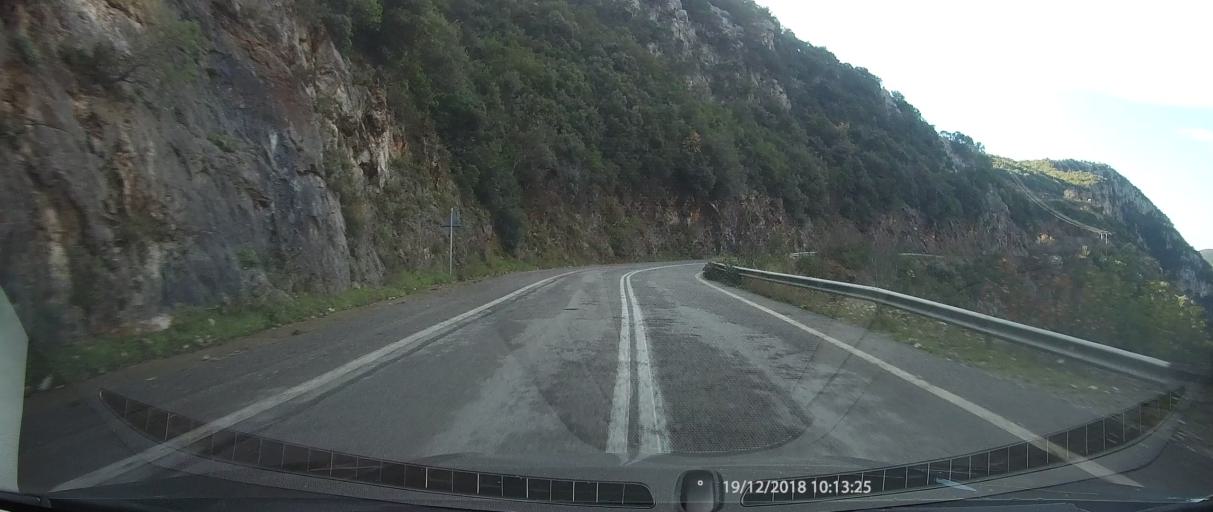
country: GR
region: Peloponnese
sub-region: Nomos Messinias
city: Kalamata
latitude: 37.0860
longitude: 22.1597
